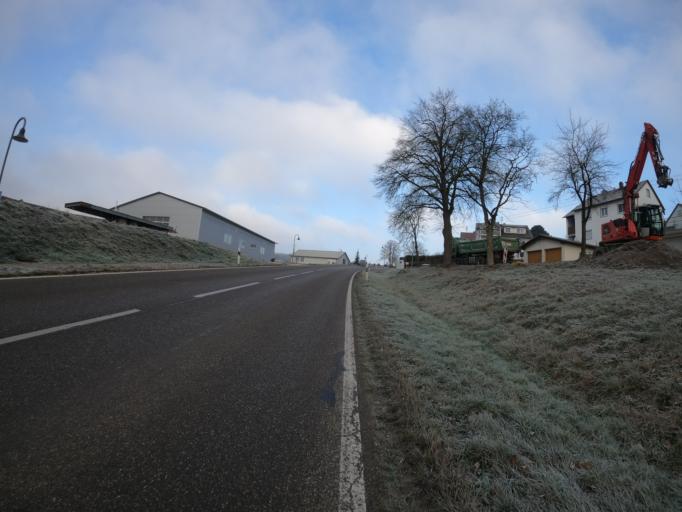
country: DE
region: Baden-Wuerttemberg
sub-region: Tuebingen Region
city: Lonsee
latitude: 48.5334
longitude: 9.9260
